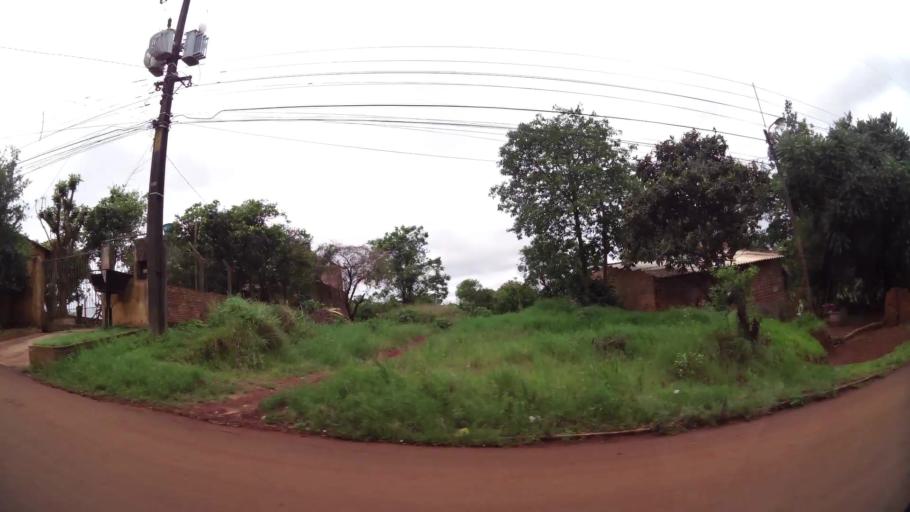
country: PY
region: Alto Parana
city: Presidente Franco
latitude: -25.5056
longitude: -54.6882
